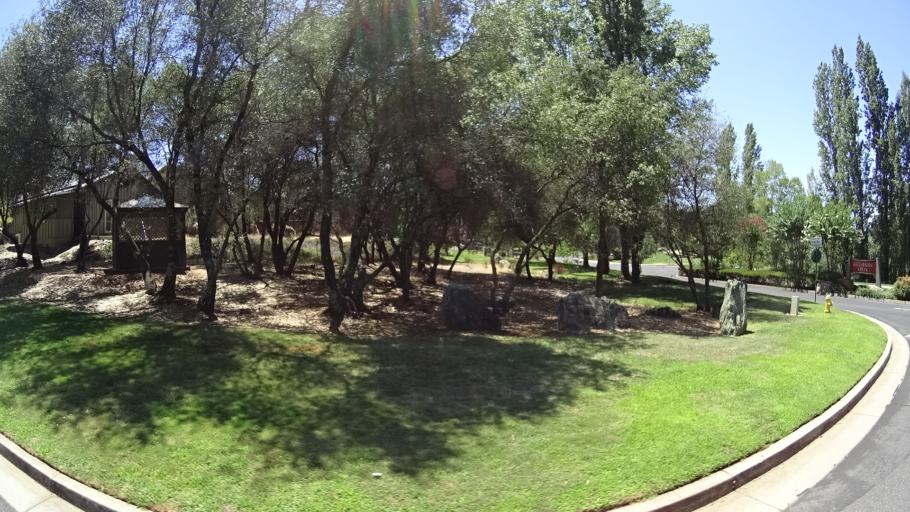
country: US
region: California
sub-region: Calaveras County
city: Angels Camp
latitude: 38.0719
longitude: -120.5569
